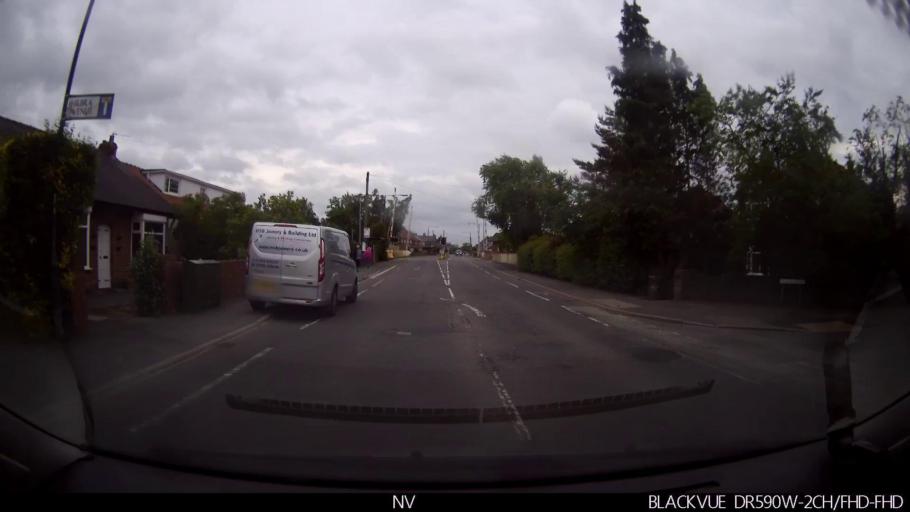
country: GB
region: England
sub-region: City of York
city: Haxby
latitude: 54.0051
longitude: -1.0738
